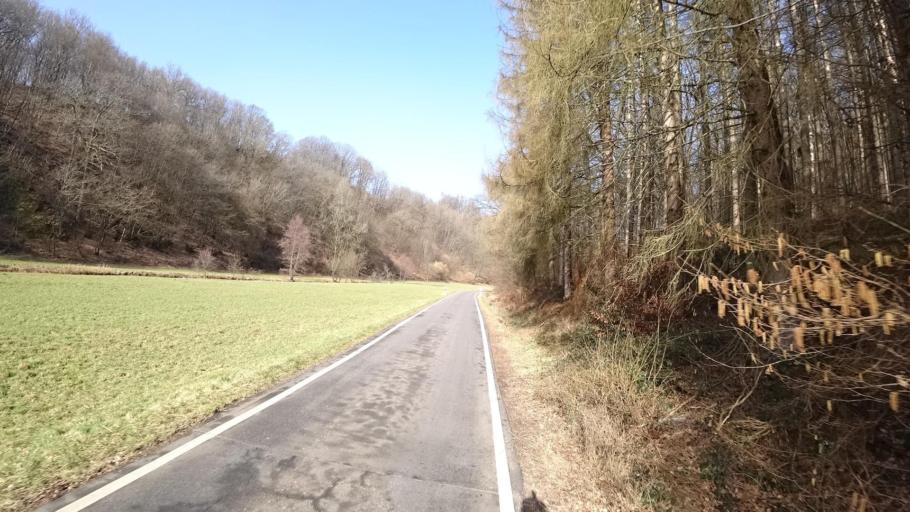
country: DE
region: Rheinland-Pfalz
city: Etzbach
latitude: 50.7800
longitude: 7.7078
